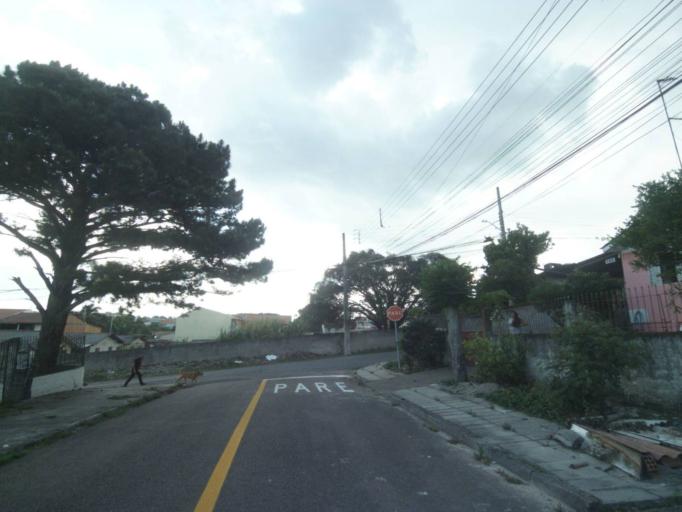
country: BR
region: Parana
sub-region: Sao Jose Dos Pinhais
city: Sao Jose dos Pinhais
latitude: -25.5293
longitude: -49.2735
